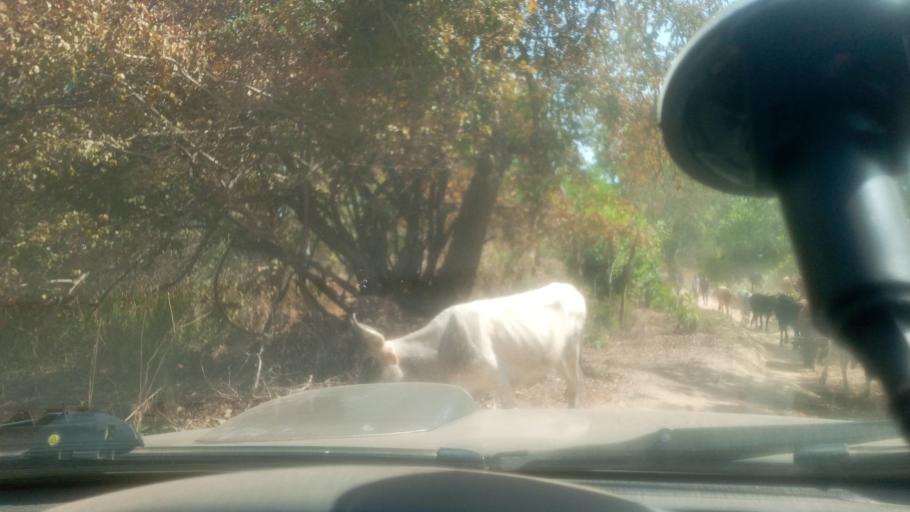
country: GW
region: Oio
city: Farim
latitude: 12.4772
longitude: -15.4067
